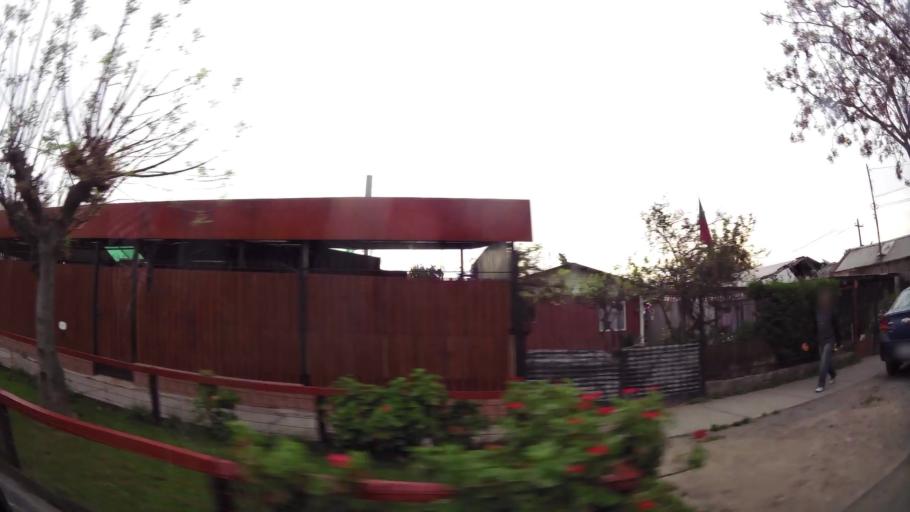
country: CL
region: Santiago Metropolitan
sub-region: Provincia de Santiago
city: Lo Prado
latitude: -33.5200
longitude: -70.7688
